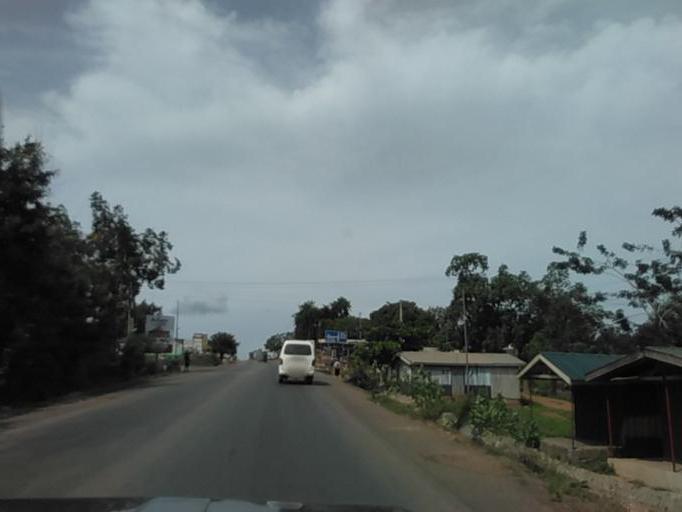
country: GH
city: Akropong
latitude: 6.2070
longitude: 0.0801
